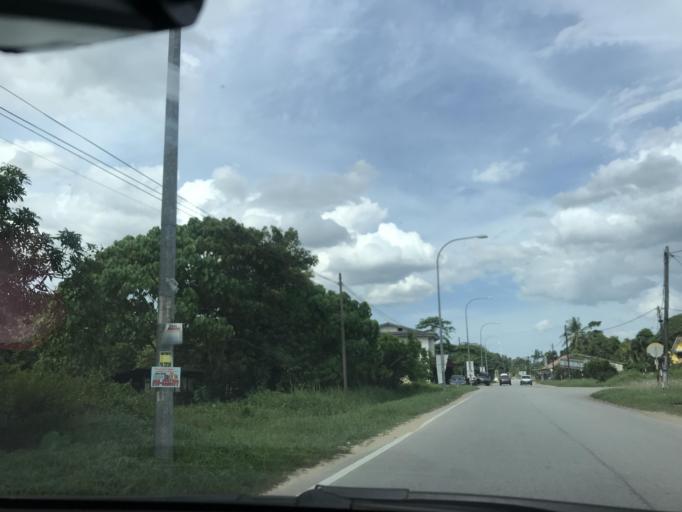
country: MY
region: Kelantan
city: Kampung Lemal
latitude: 6.0337
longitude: 102.1602
